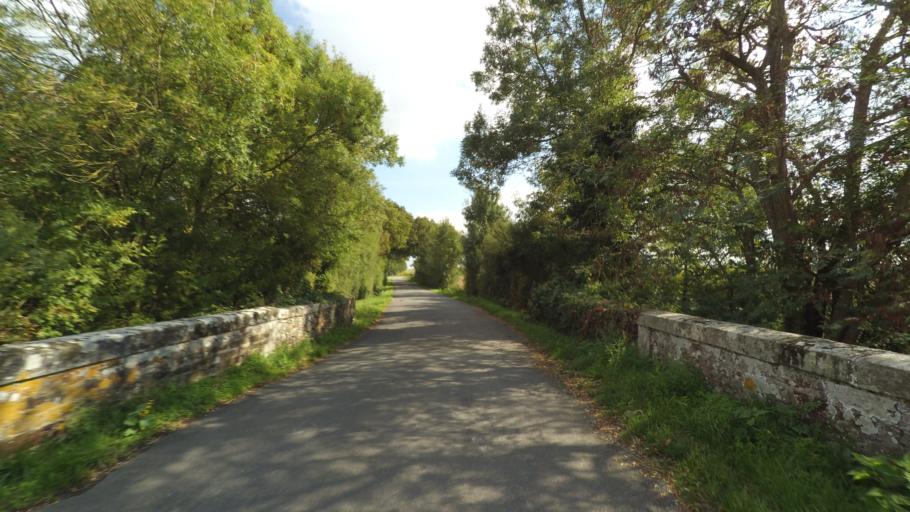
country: FR
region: Pays de la Loire
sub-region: Departement de la Vendee
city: Bouffere
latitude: 46.9521
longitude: -1.3732
